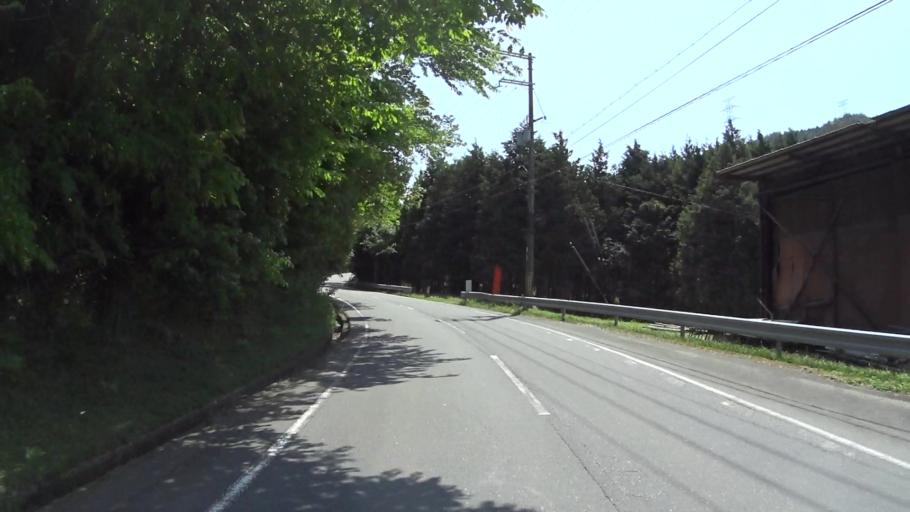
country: JP
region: Kyoto
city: Kameoka
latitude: 34.9971
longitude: 135.4778
